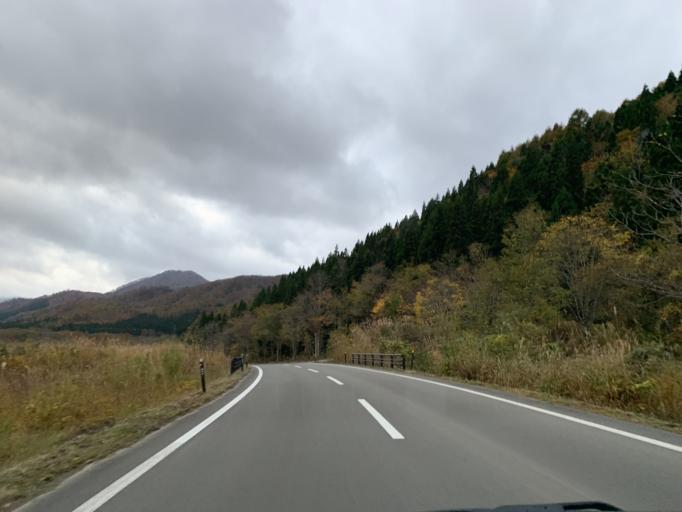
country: JP
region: Iwate
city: Mizusawa
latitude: 39.0924
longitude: 140.8643
